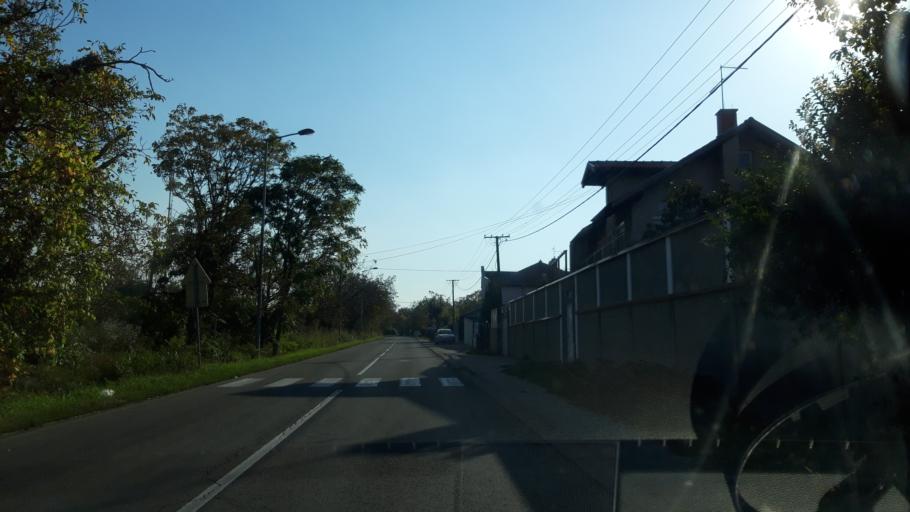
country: RS
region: Autonomna Pokrajina Vojvodina
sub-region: Juznobacki Okrug
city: Petrovaradin
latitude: 45.2402
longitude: 19.8665
